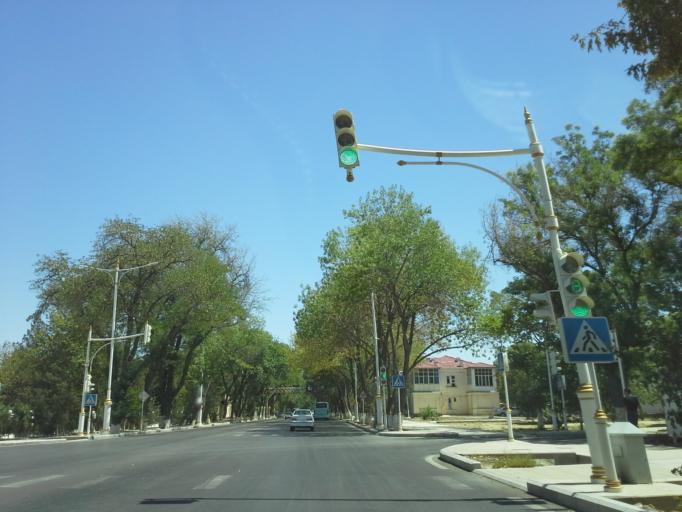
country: TM
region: Ahal
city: Ashgabat
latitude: 37.9336
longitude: 58.4040
